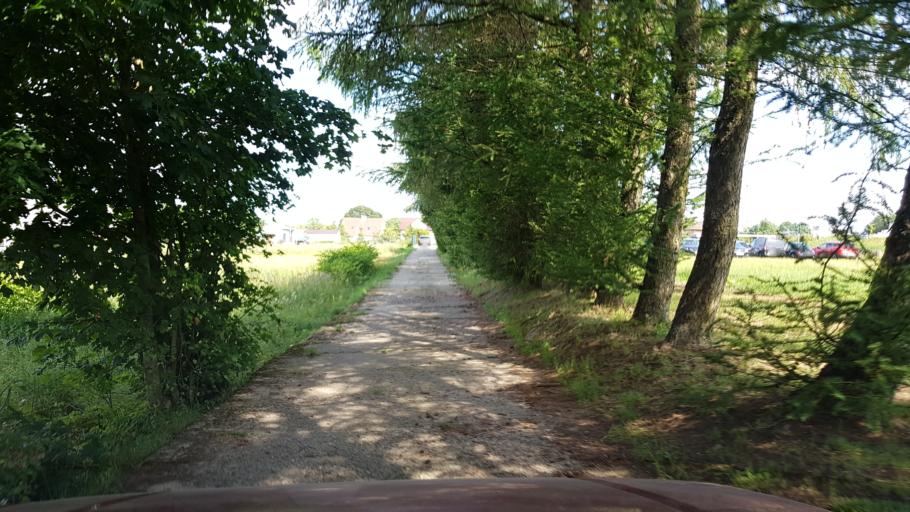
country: PL
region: West Pomeranian Voivodeship
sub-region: Powiat koszalinski
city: Polanow
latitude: 54.1733
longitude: 16.5972
